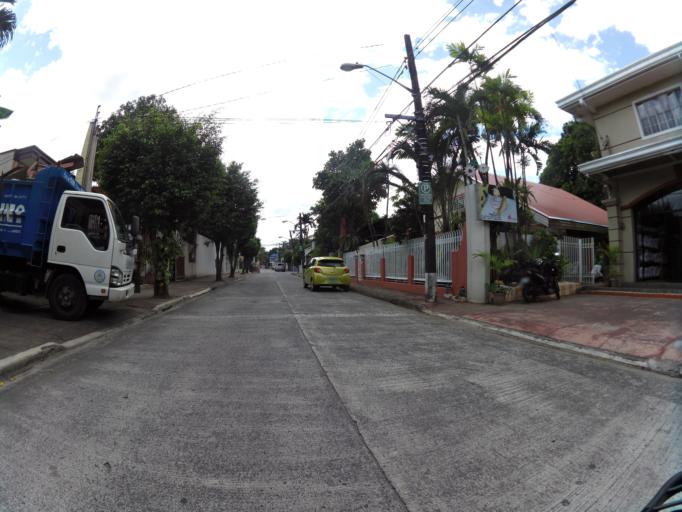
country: PH
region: Metro Manila
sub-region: Marikina
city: Calumpang
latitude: 14.6302
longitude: 121.0999
